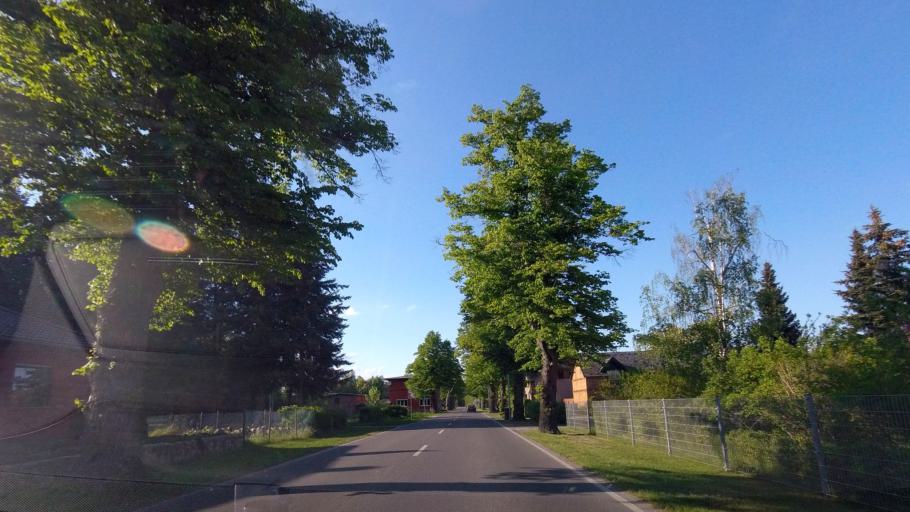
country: DE
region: Brandenburg
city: Luebben
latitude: 51.8885
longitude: 13.9011
